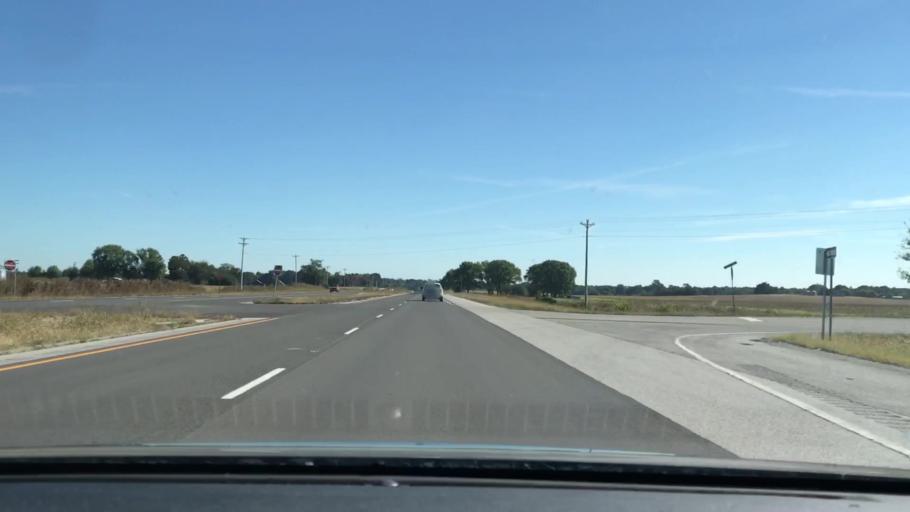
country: US
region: Kentucky
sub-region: Todd County
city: Elkton
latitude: 36.8122
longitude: -87.0312
